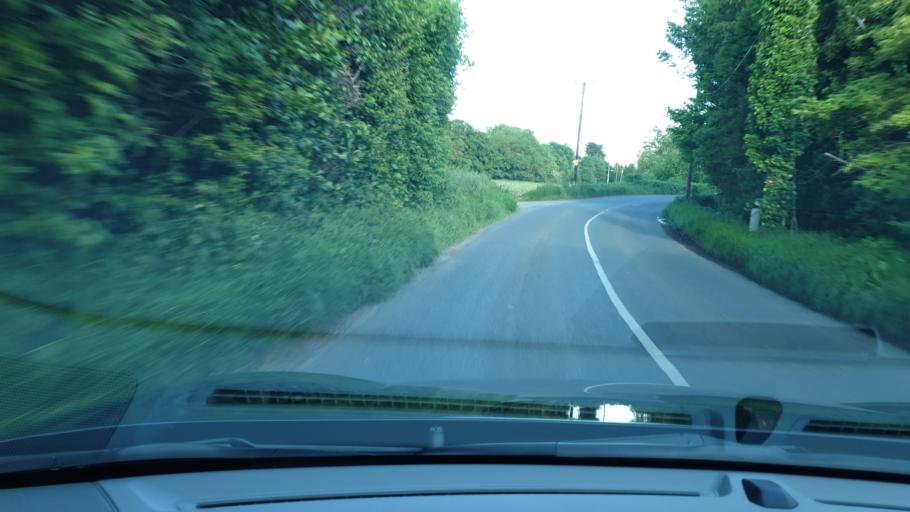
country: IE
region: Leinster
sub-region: An Mhi
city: Ashbourne
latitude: 53.5337
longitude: -6.3127
